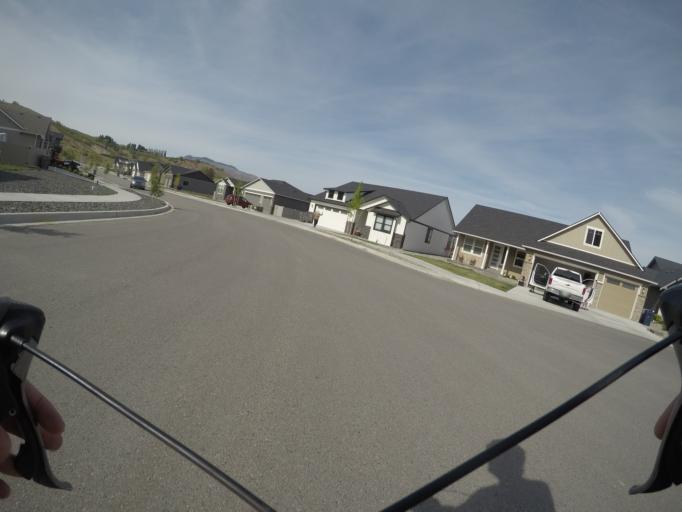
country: US
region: Washington
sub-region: Chelan County
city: West Wenatchee
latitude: 47.4351
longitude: -120.3551
